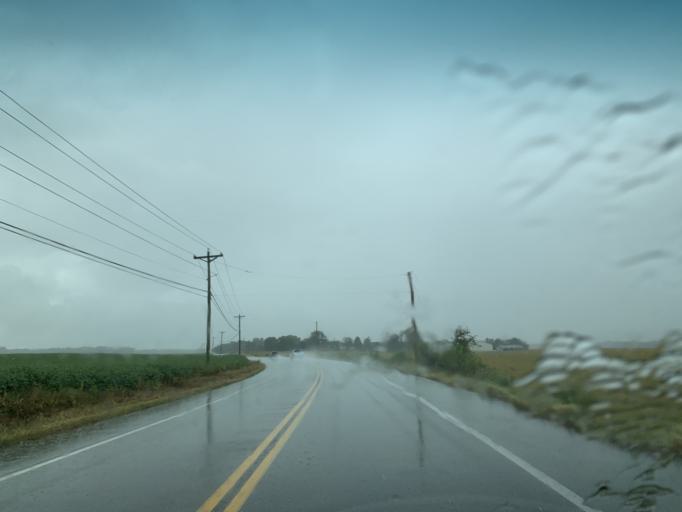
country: US
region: Maryland
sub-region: Queen Anne's County
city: Kingstown
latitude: 39.2113
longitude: -75.8633
